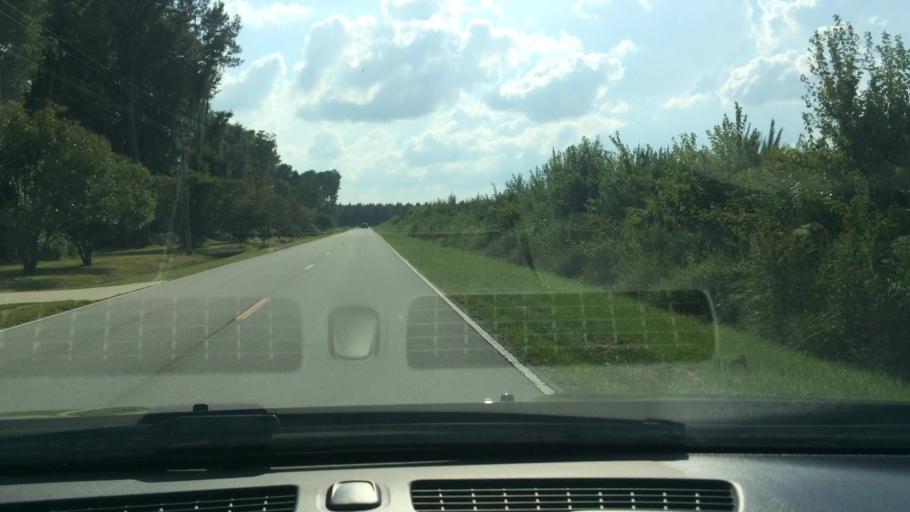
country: US
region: North Carolina
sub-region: Beaufort County
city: River Road
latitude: 35.4364
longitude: -77.0034
